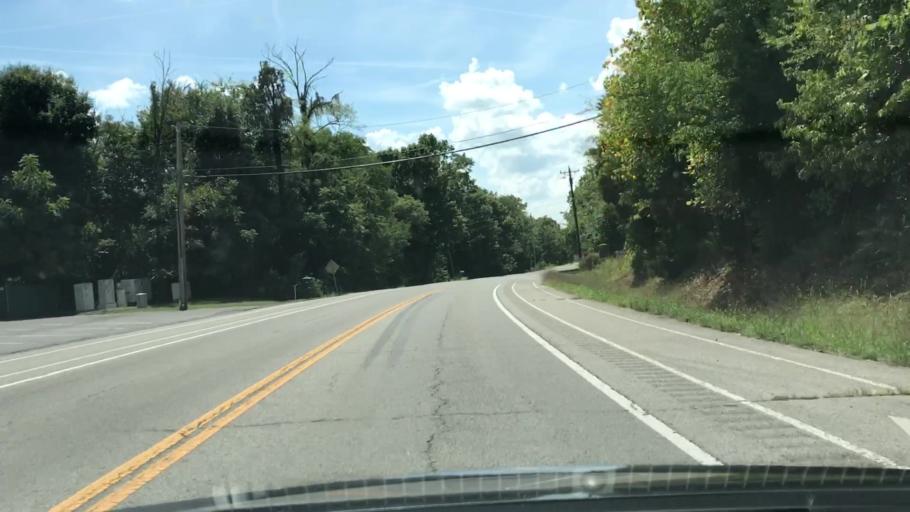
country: US
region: Tennessee
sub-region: Sumner County
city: White House
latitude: 36.4960
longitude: -86.6408
